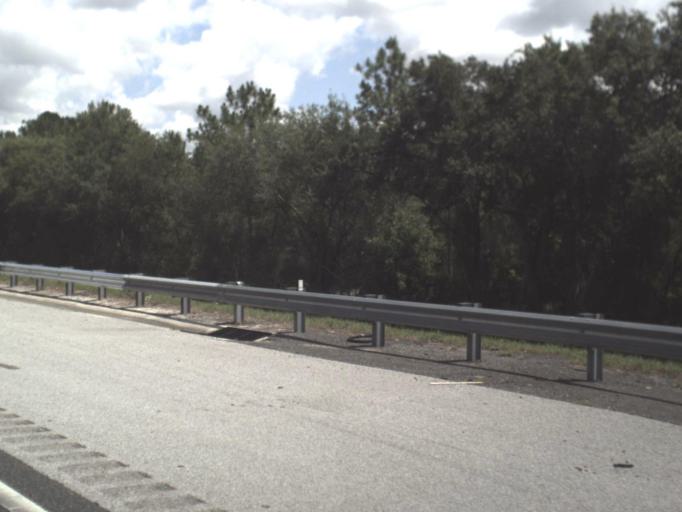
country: US
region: Florida
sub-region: Suwannee County
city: Wellborn
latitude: 30.3406
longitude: -82.8280
